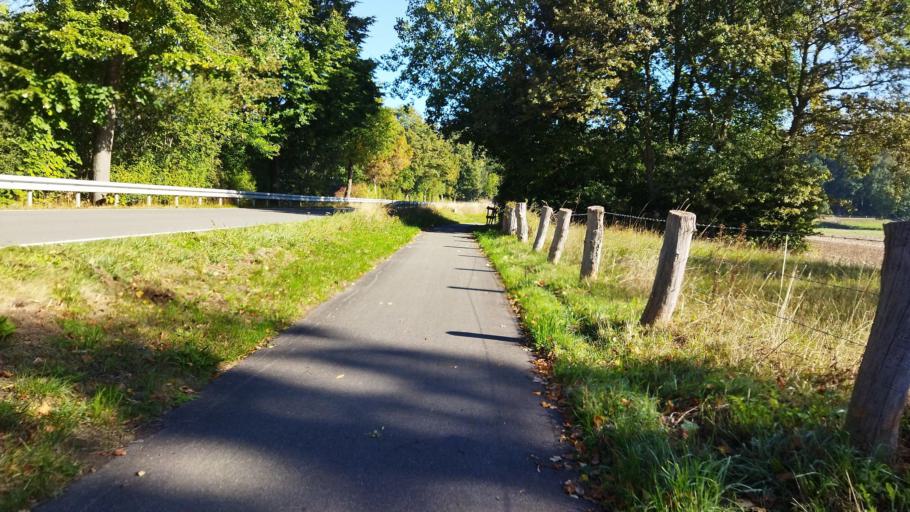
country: DE
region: North Rhine-Westphalia
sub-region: Regierungsbezirk Munster
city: Wettringen
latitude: 52.2442
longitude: 7.3124
